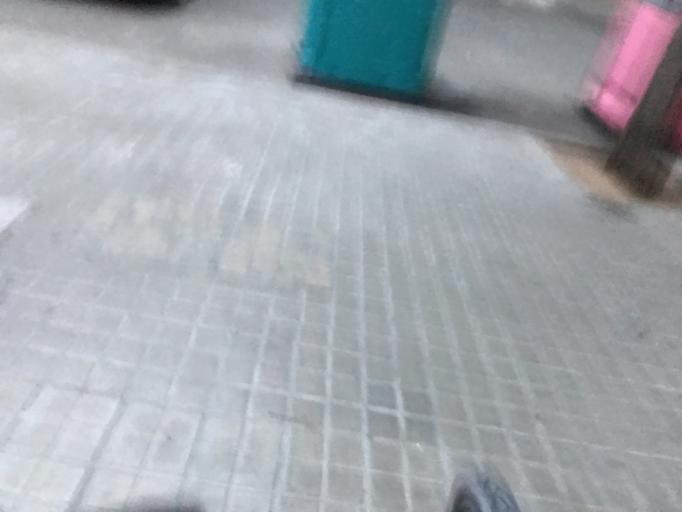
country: ES
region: Valencia
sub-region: Provincia de Valencia
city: Valencia
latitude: 39.4750
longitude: -0.3791
